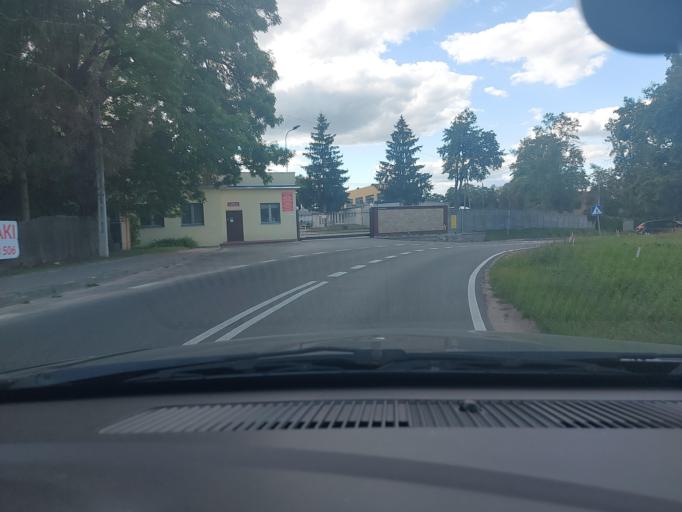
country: PL
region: Masovian Voivodeship
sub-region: Powiat nowodworski
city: Pomiechowek
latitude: 52.4744
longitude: 20.7262
